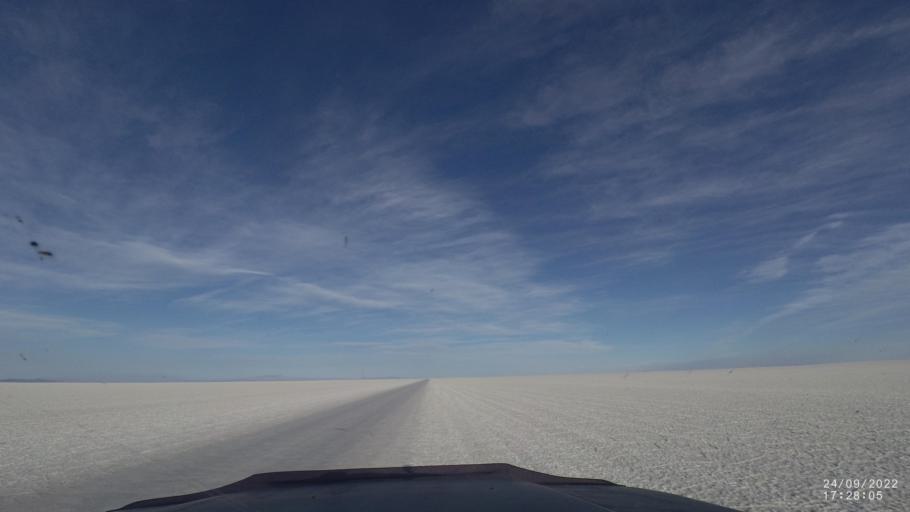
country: BO
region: Potosi
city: Colchani
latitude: -20.3020
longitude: -67.4347
